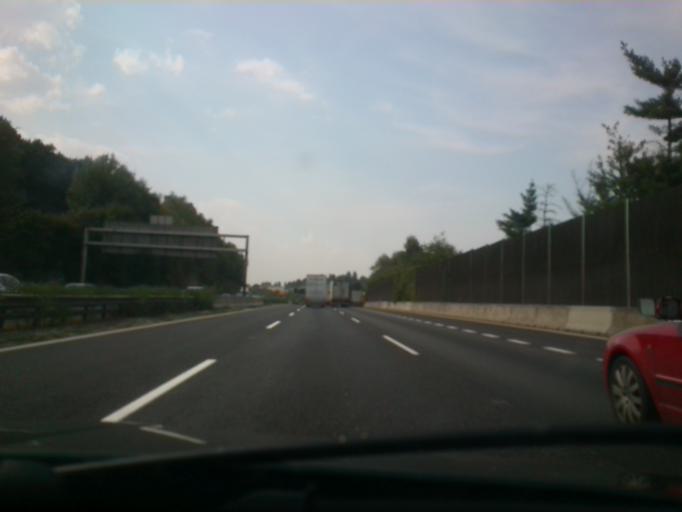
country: CZ
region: Central Bohemia
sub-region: Okres Praha-Vychod
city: Mnichovice
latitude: 49.9294
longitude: 14.6965
